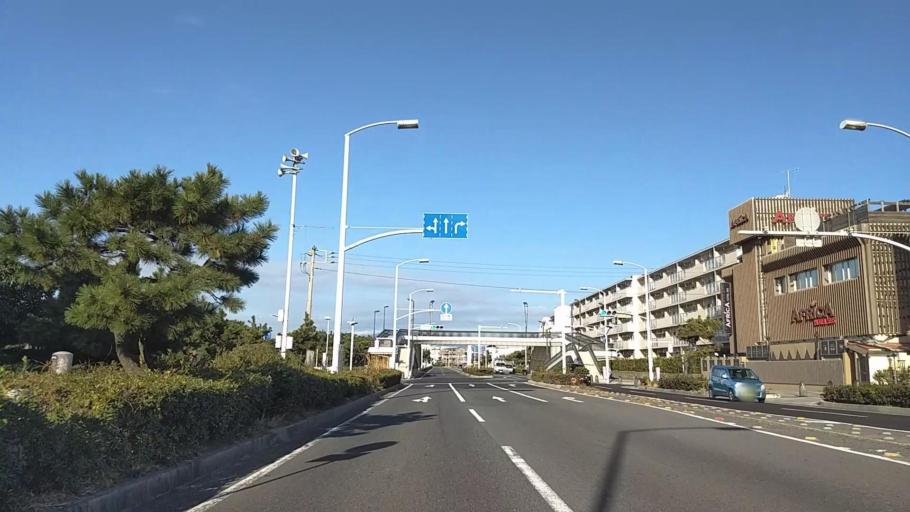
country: JP
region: Kanagawa
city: Fujisawa
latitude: 35.3148
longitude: 139.4744
